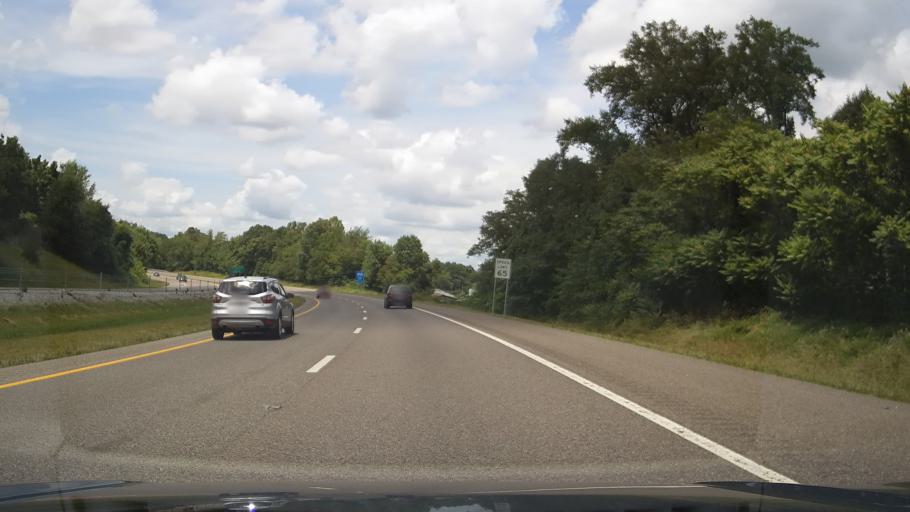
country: US
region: Tennessee
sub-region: Carter County
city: Pine Crest
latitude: 36.2781
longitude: -82.3185
